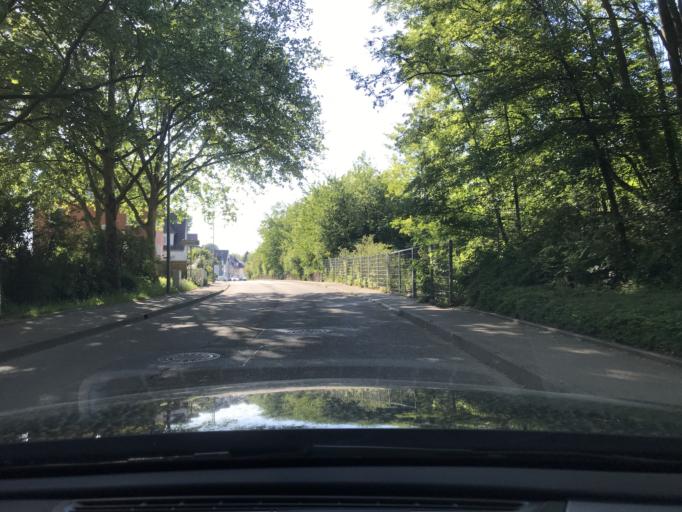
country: DE
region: Baden-Wuerttemberg
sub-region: Regierungsbezirk Stuttgart
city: Weinstadt-Endersbach
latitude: 48.8226
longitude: 9.3419
